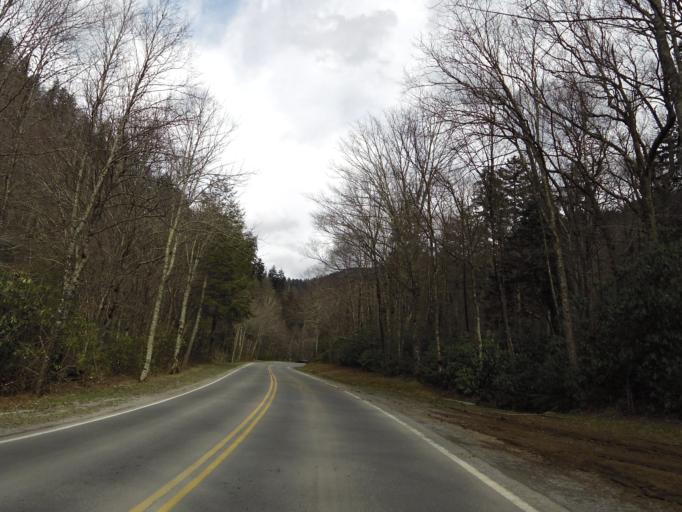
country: US
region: Tennessee
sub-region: Sevier County
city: Gatlinburg
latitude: 35.6183
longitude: -83.4308
